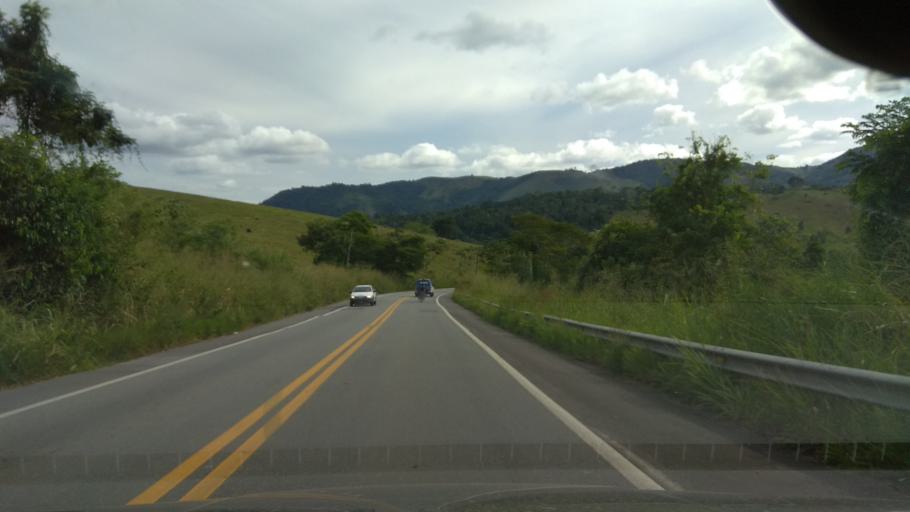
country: BR
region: Bahia
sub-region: Jitauna
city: Jitauna
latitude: -14.0077
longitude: -39.9122
